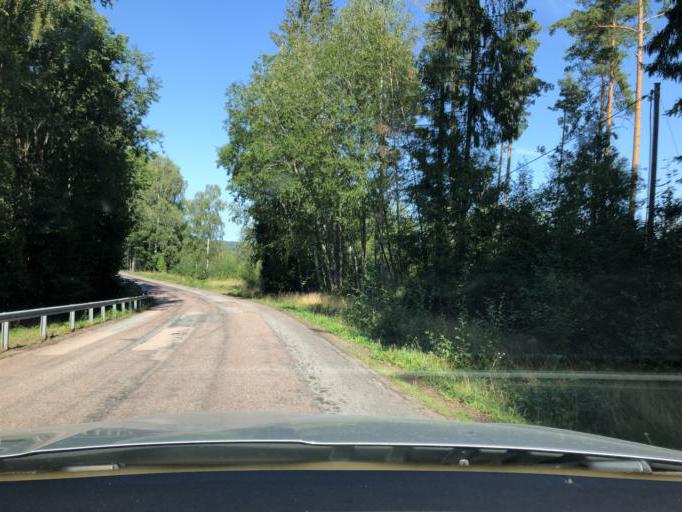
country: SE
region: Dalarna
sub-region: Hedemora Kommun
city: Hedemora
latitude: 60.3273
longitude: 15.9162
